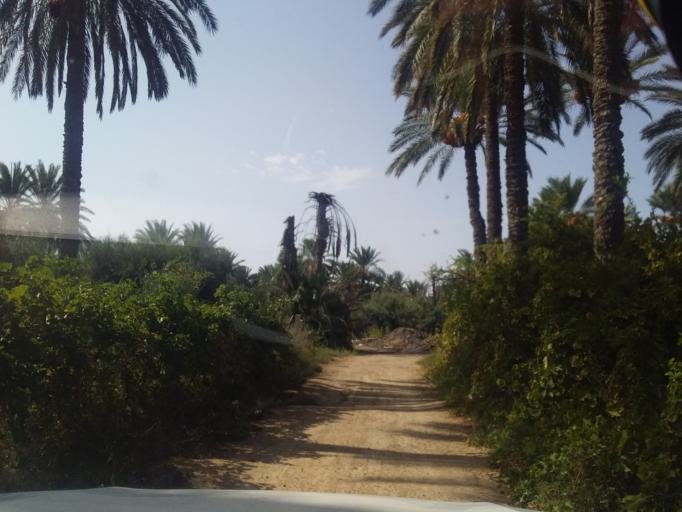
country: TN
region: Qabis
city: Gabes
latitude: 33.6272
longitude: 10.2856
